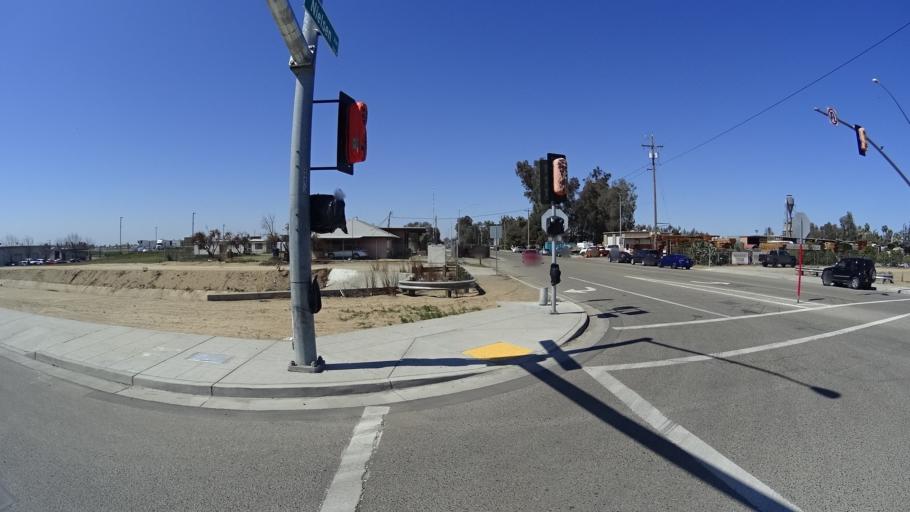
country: US
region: California
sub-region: Fresno County
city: West Park
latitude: 36.7428
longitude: -119.8444
